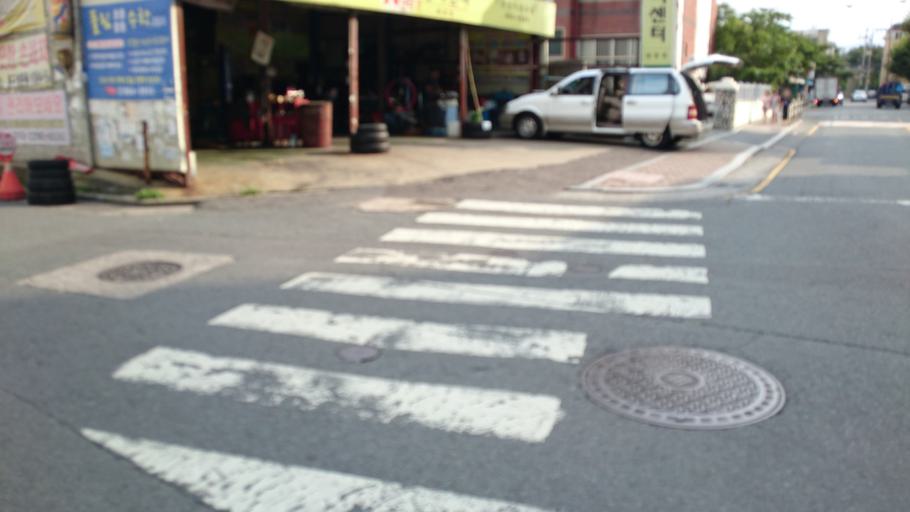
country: KR
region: Daegu
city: Daegu
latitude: 35.8803
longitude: 128.6615
